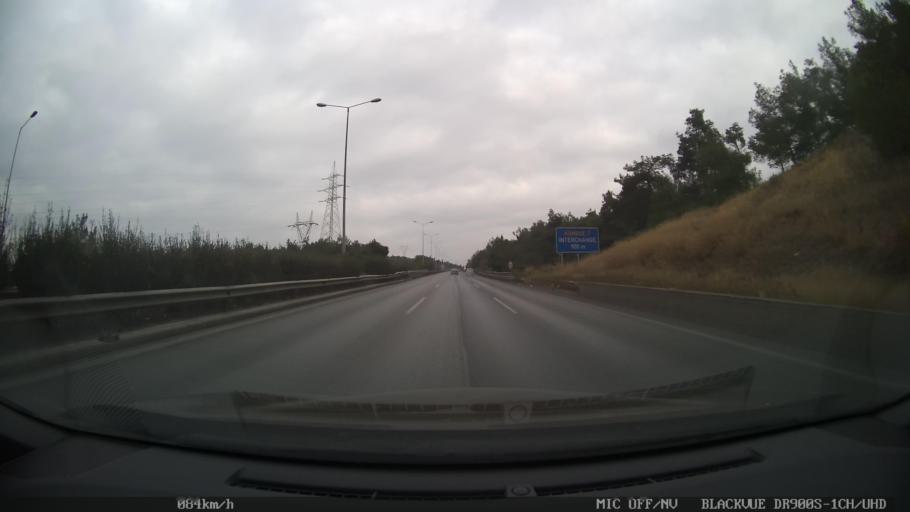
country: GR
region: Central Macedonia
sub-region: Nomos Thessalonikis
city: Agios Pavlos
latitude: 40.6359
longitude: 22.9720
